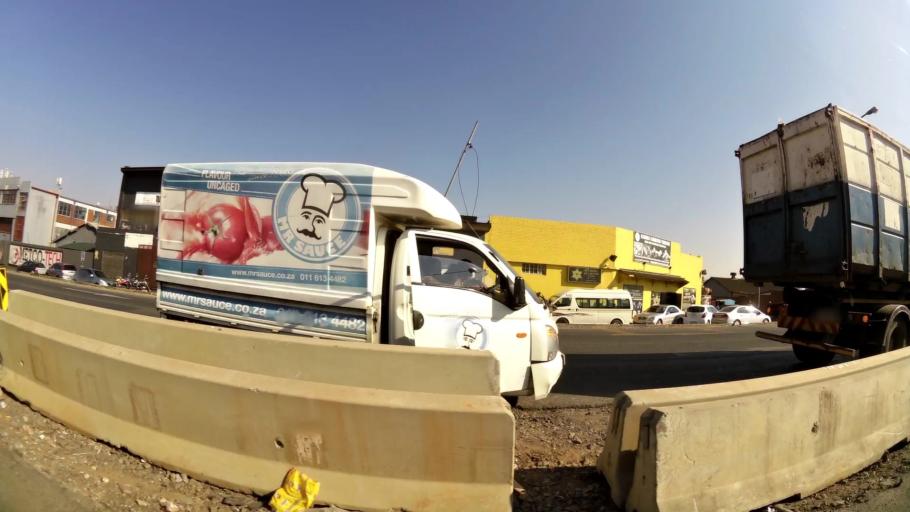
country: ZA
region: Gauteng
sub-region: City of Johannesburg Metropolitan Municipality
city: Modderfontein
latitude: -26.1047
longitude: 28.0854
